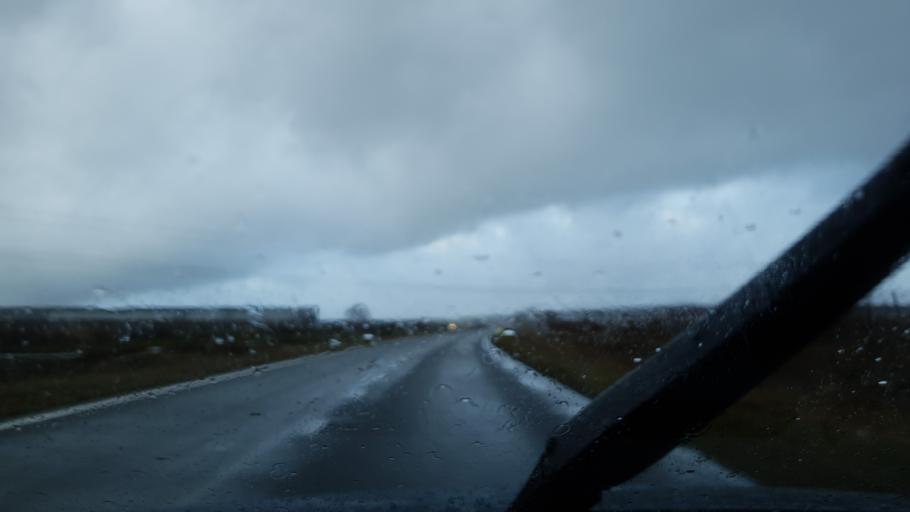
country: NL
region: Limburg
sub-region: Gemeente Venlo
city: Tegelen
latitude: 51.4112
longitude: 6.1077
